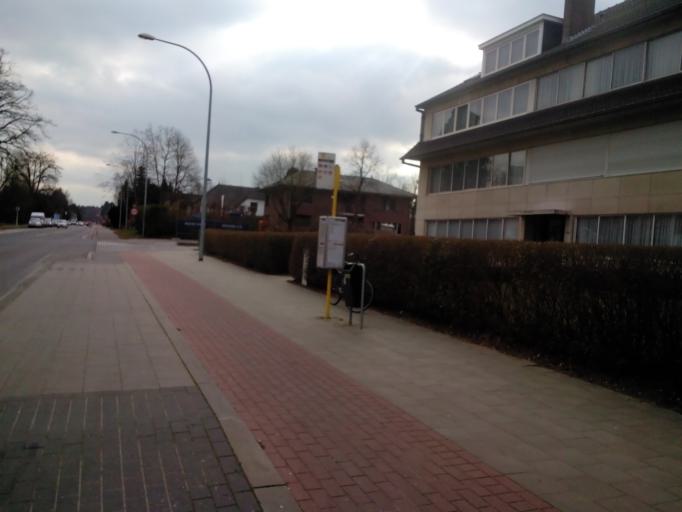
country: BE
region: Flanders
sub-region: Provincie Vlaams-Brabant
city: Leuven
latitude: 50.8556
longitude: 4.6957
